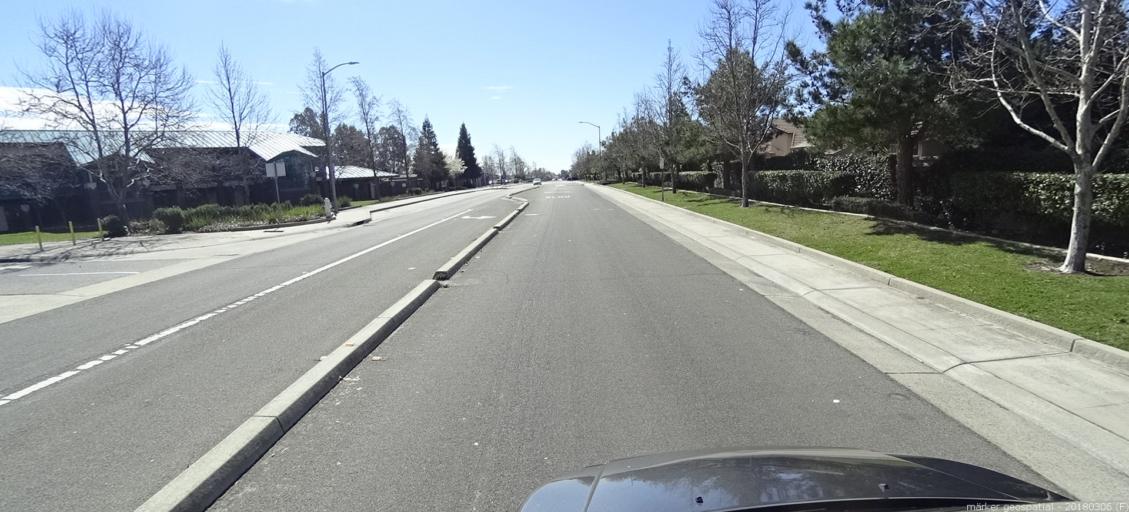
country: US
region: California
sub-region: Sacramento County
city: Vineyard
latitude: 38.4571
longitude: -121.3487
